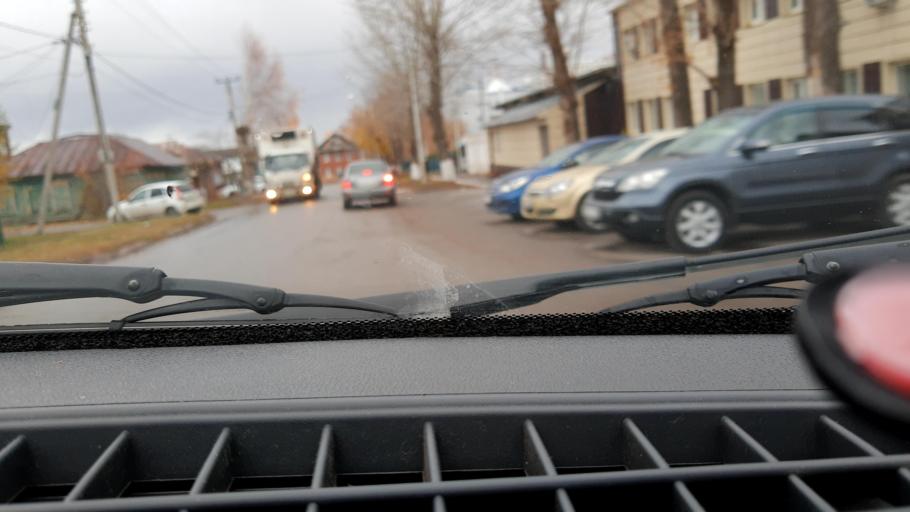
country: RU
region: Bashkortostan
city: Ufa
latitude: 54.7243
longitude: 55.9218
